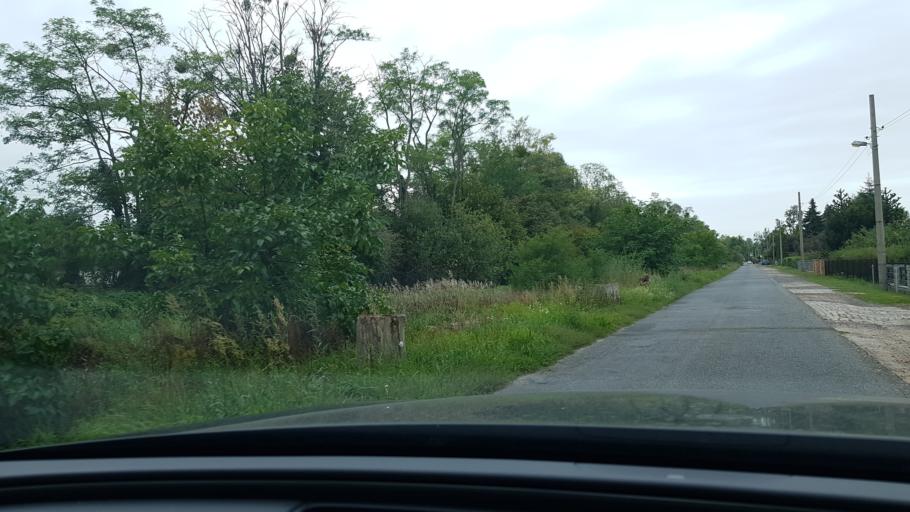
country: DE
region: Brandenburg
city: Brieselang
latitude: 52.5870
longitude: 12.9859
